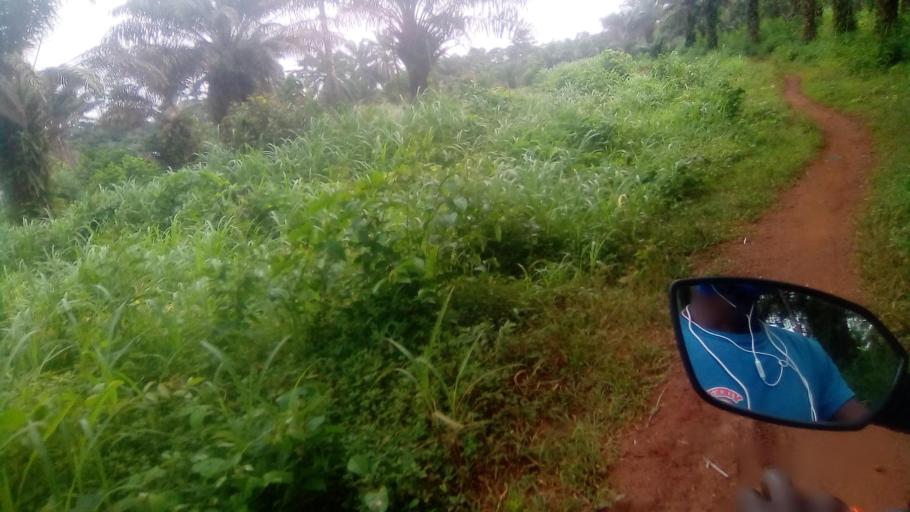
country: SL
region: Eastern Province
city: Kailahun
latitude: 8.2680
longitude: -10.5596
